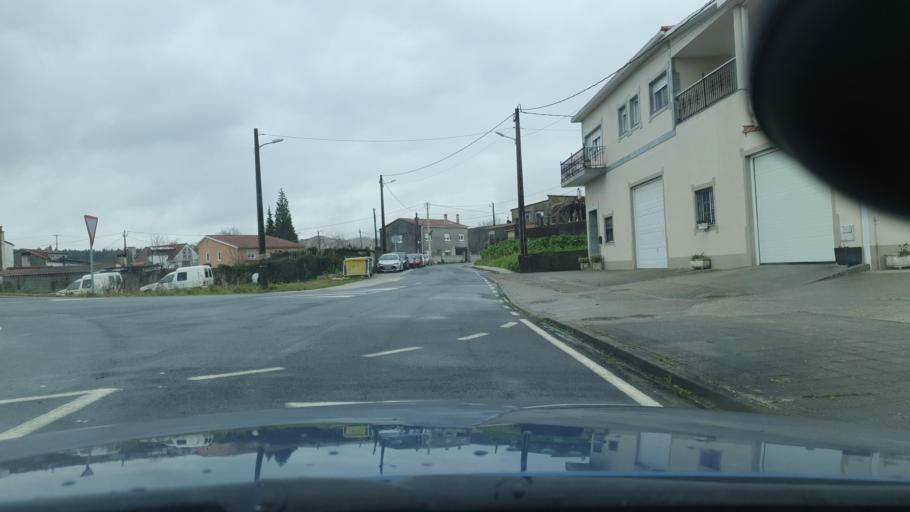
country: ES
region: Galicia
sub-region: Provincia da Coruna
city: Ames
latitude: 42.8271
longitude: -8.6129
